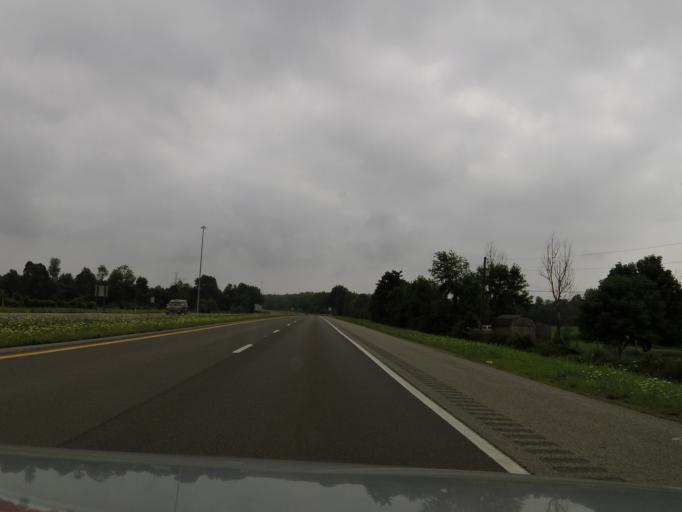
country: US
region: Kentucky
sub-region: Muhlenberg County
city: Greenville
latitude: 37.2365
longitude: -87.2644
